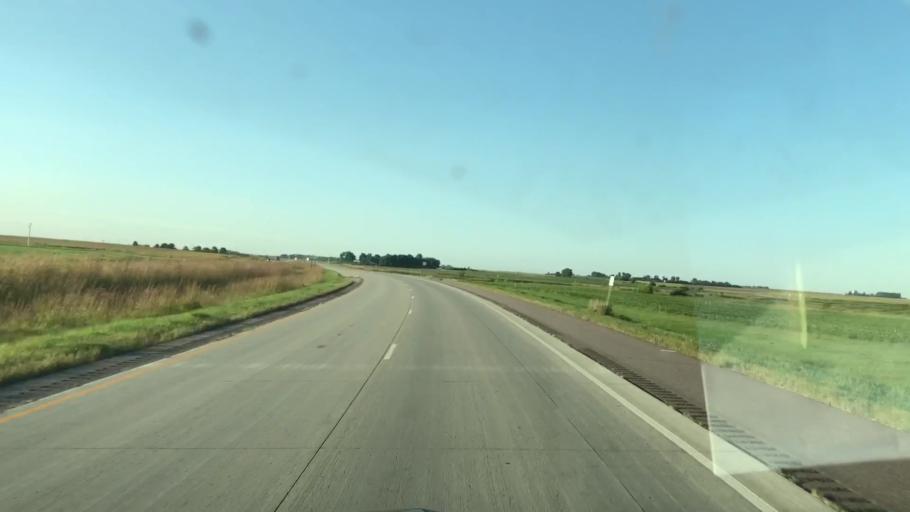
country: US
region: Minnesota
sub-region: Nobles County
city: Worthington
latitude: 43.5758
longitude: -95.6535
